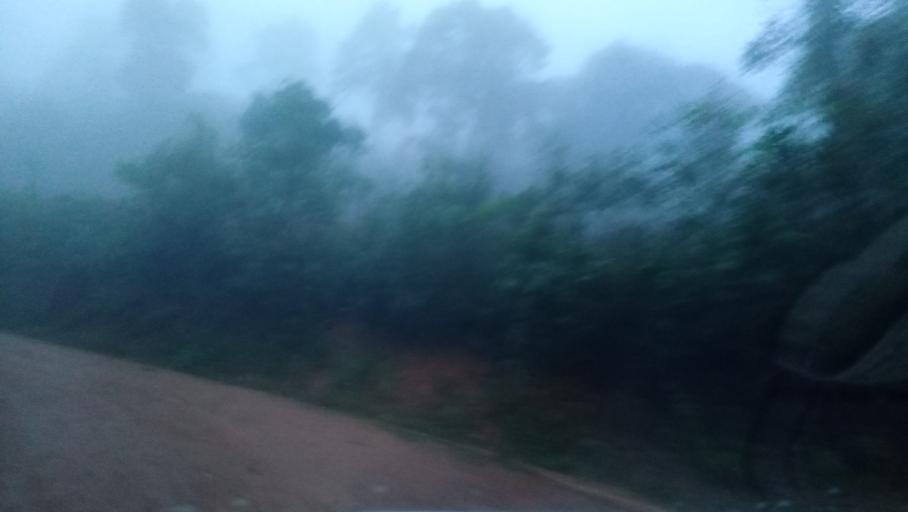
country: LA
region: Phongsali
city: Khoa
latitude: 21.2148
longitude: 102.2327
